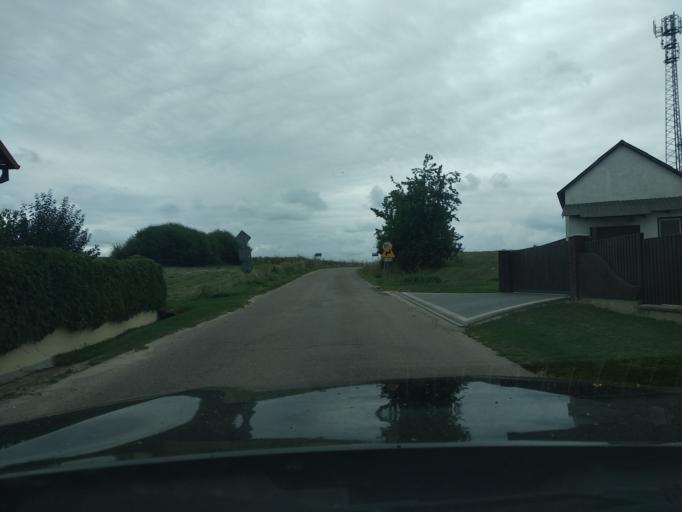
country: PL
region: Masovian Voivodeship
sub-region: Powiat pultuski
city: Obryte
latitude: 52.7552
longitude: 21.2169
